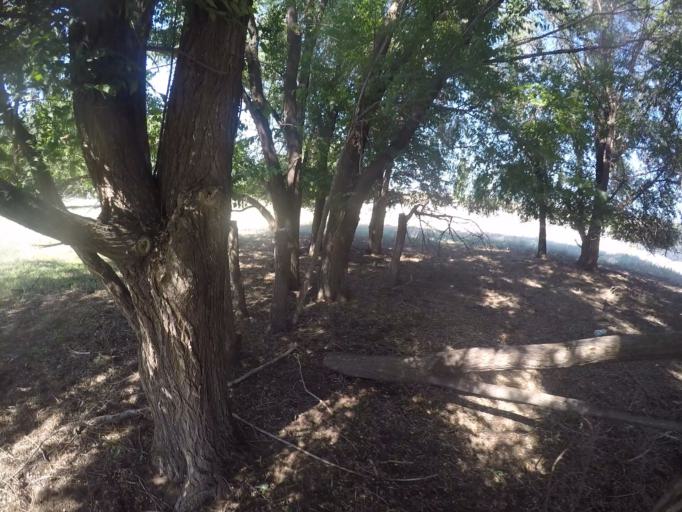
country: RU
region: Saratov
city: Privolzhskiy
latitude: 51.1781
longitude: 45.9172
